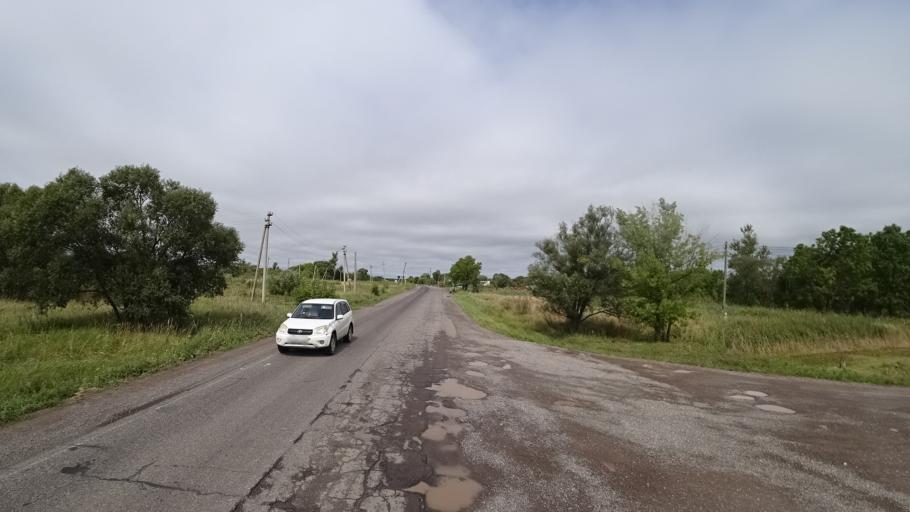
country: RU
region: Primorskiy
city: Monastyrishche
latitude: 44.1946
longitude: 132.4799
